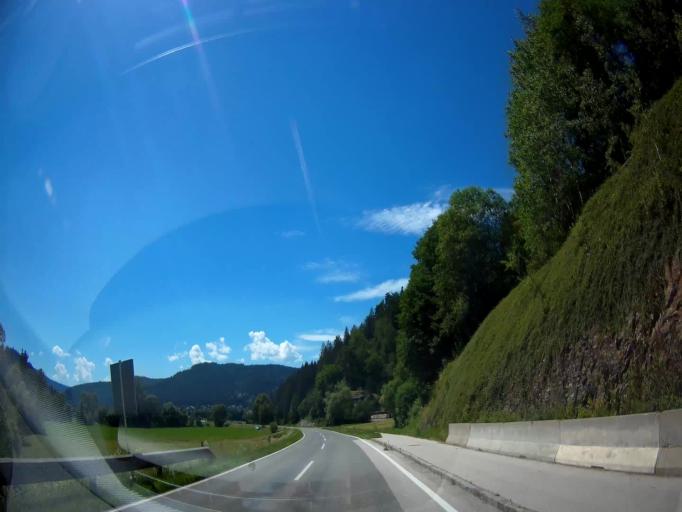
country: AT
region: Carinthia
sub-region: Politischer Bezirk Sankt Veit an der Glan
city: Gurk
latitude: 46.8644
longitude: 14.2459
